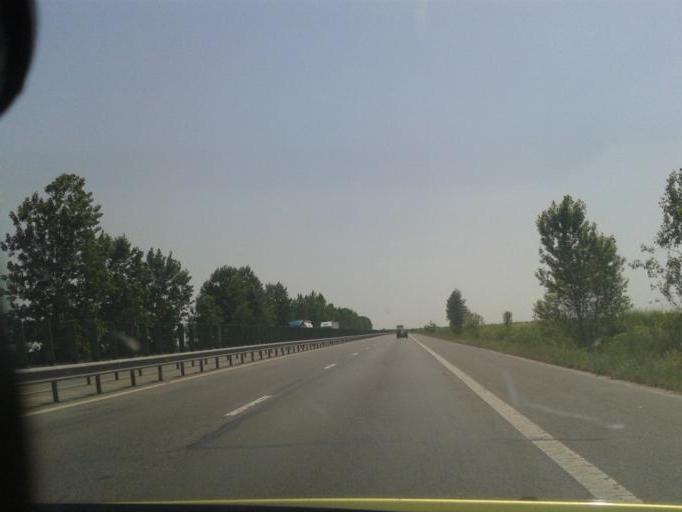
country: RO
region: Calarasi
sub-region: Comuna Tamadau Mare
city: Tamadau Mare
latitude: 44.4458
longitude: 26.5429
